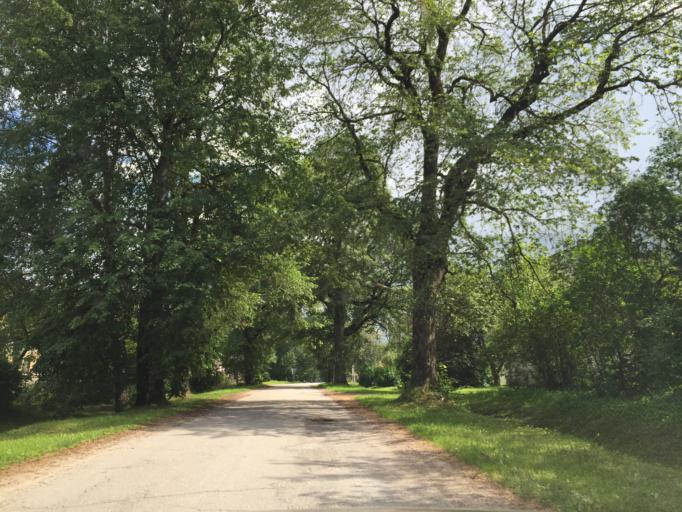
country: LV
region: Malpils
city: Malpils
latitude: 56.8594
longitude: 25.0197
